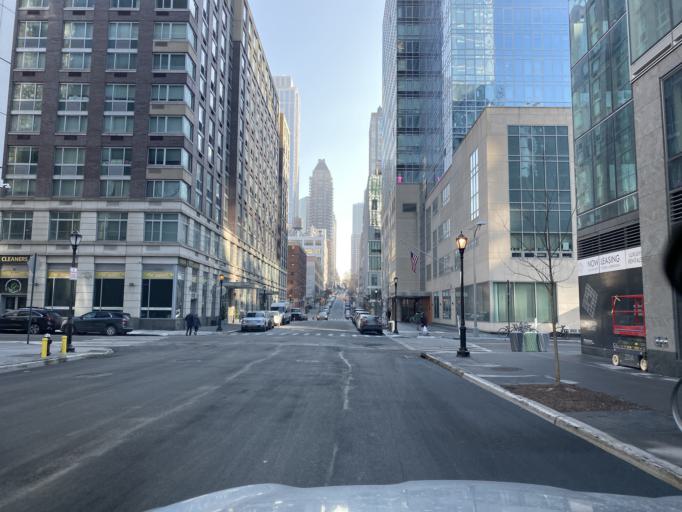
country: US
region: New Jersey
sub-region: Hudson County
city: Guttenberg
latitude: 40.7734
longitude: -73.9909
